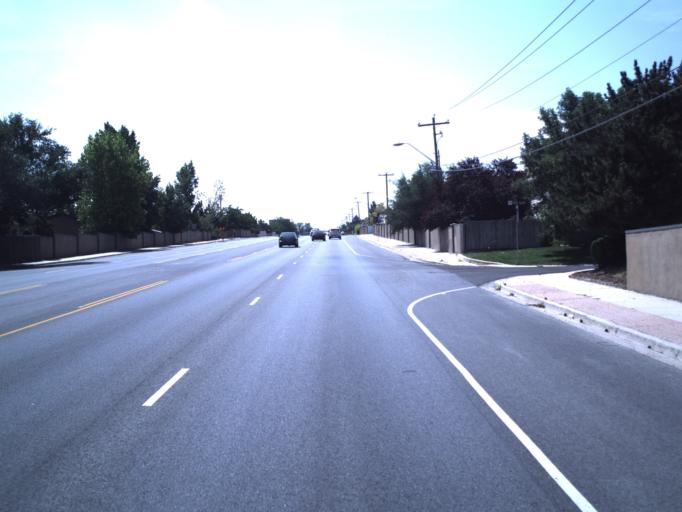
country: US
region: Utah
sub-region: Salt Lake County
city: West Valley City
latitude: 40.6763
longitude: -112.0248
